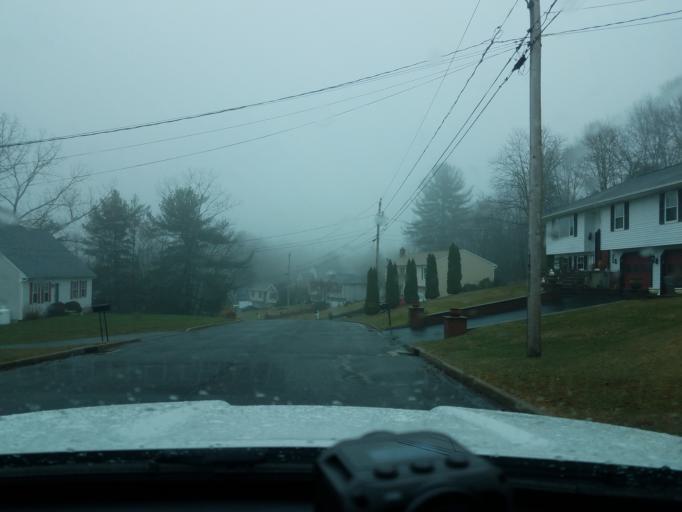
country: US
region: Connecticut
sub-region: New Haven County
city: Naugatuck
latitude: 41.4909
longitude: -73.0313
